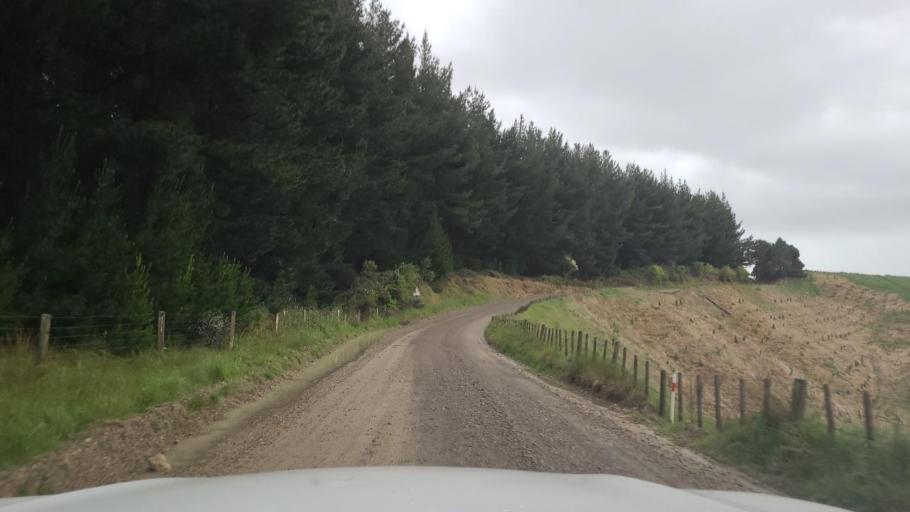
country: NZ
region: Hawke's Bay
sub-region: Napier City
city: Napier
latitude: -39.2916
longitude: 176.9066
